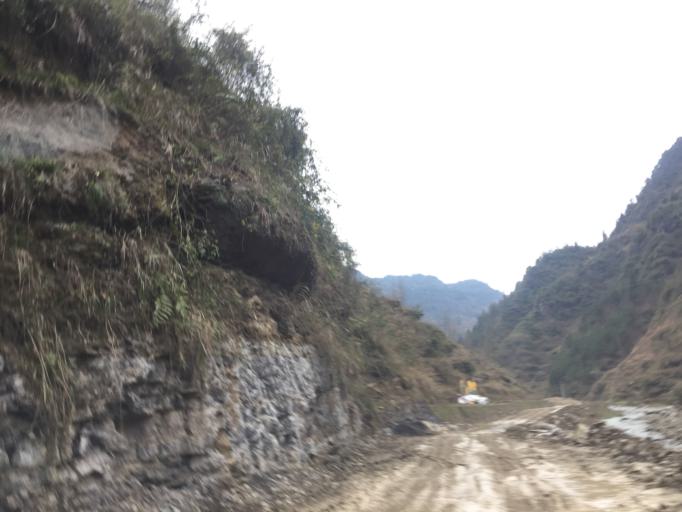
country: CN
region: Guizhou Sheng
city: Changfeng
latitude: 28.4656
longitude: 108.0811
